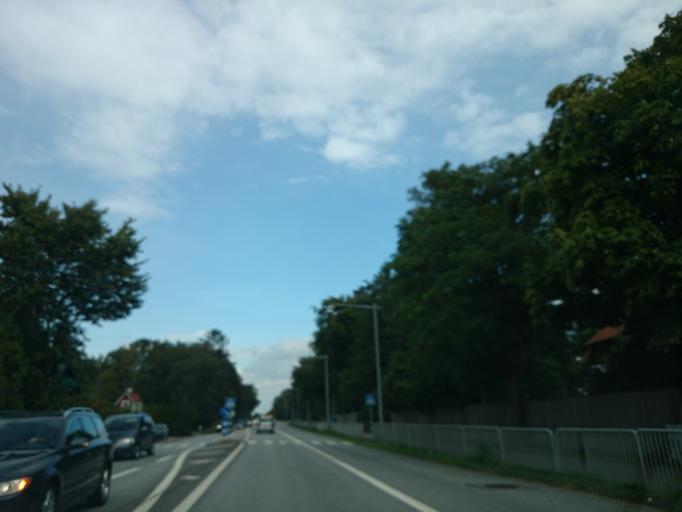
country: SE
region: Skane
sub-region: Vellinge Kommun
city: Ljunghusen
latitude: 55.4067
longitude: 12.9273
